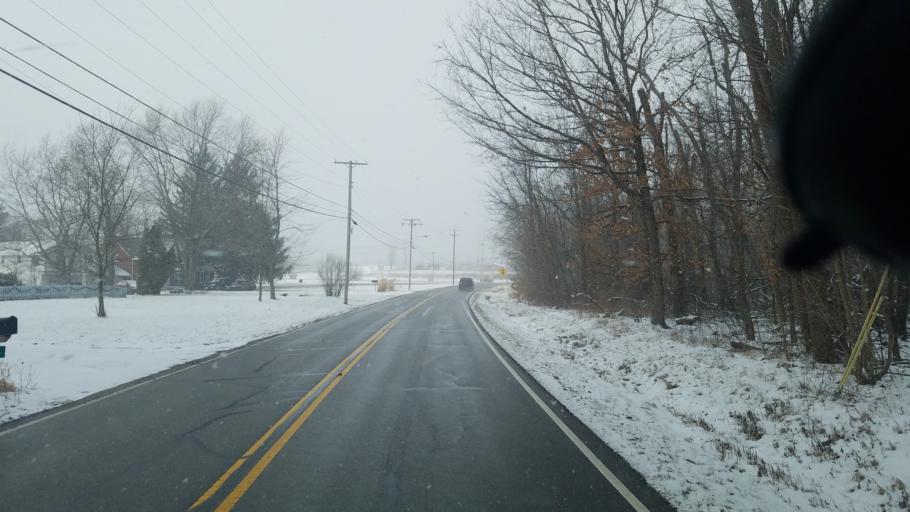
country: US
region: Ohio
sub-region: Richland County
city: Ontario
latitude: 40.7772
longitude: -82.6509
